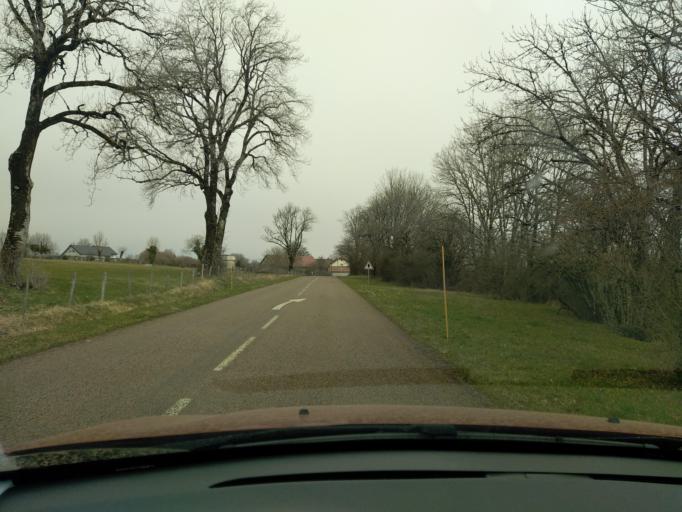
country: FR
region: Franche-Comte
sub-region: Departement du Jura
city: Champagnole
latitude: 46.7719
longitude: 5.8831
